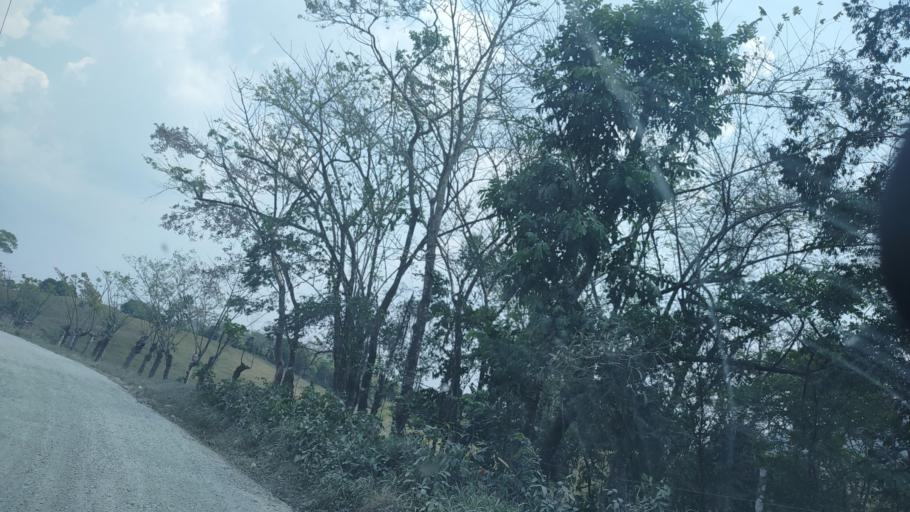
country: MX
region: Tabasco
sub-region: Huimanguillo
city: Francisco Rueda
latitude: 17.6109
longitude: -93.9133
